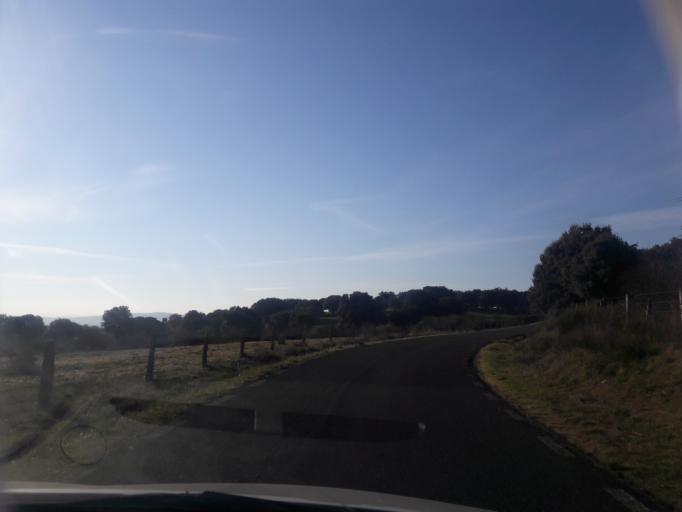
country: ES
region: Castille and Leon
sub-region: Provincia de Salamanca
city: Montejo
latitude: 40.6209
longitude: -5.6086
